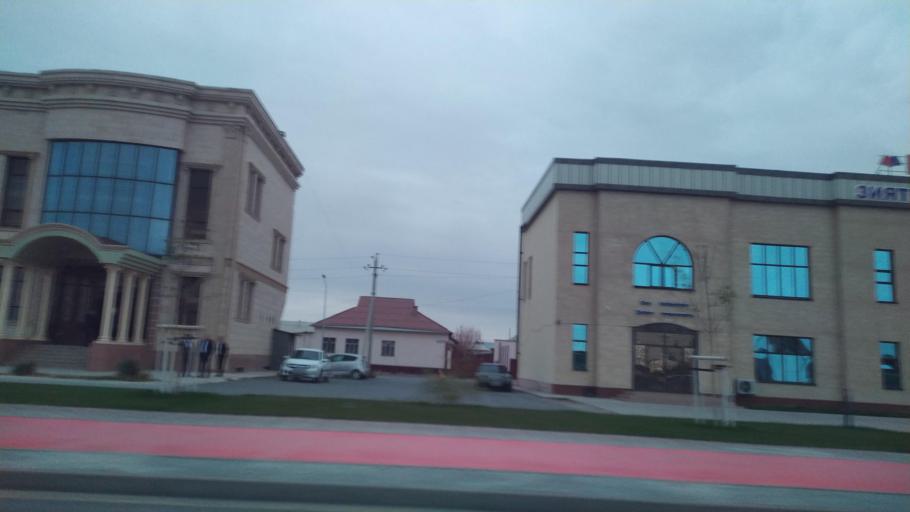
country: KZ
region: Ongtustik Qazaqstan
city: Turkestan
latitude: 43.2798
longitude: 68.3228
